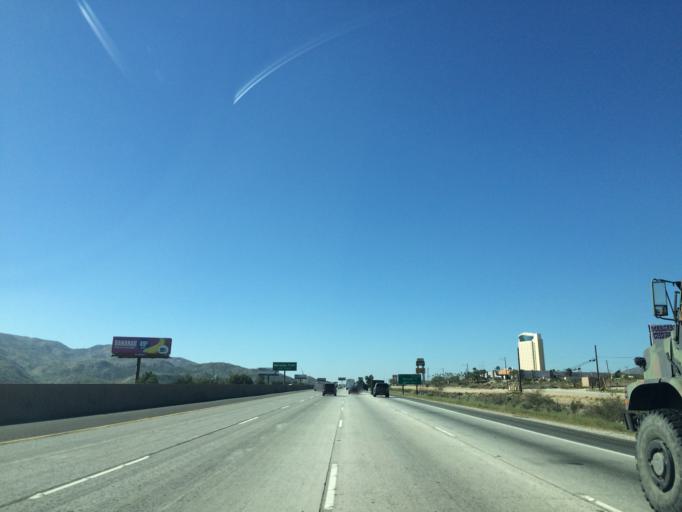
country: US
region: California
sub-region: Riverside County
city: Cabazon
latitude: 33.9189
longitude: -116.7876
